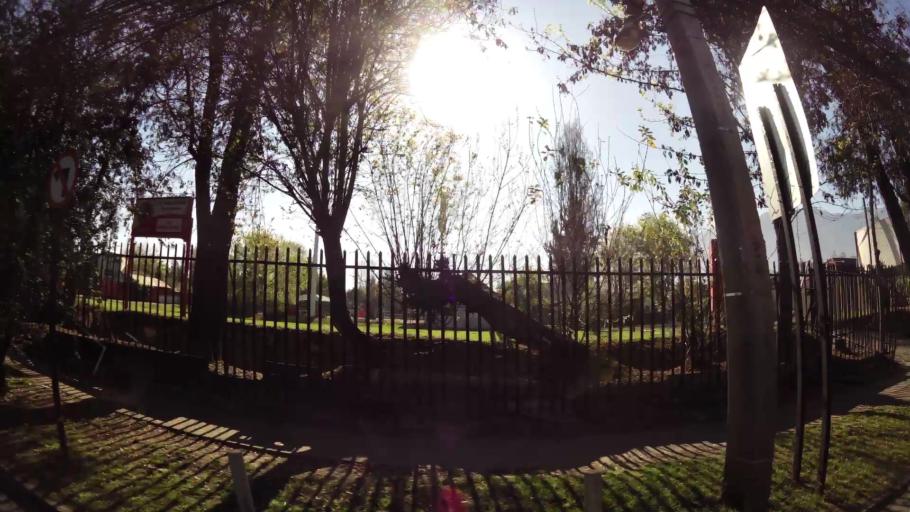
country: CL
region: Santiago Metropolitan
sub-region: Provincia de Santiago
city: Villa Presidente Frei, Nunoa, Santiago, Chile
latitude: -33.4454
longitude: -70.5517
